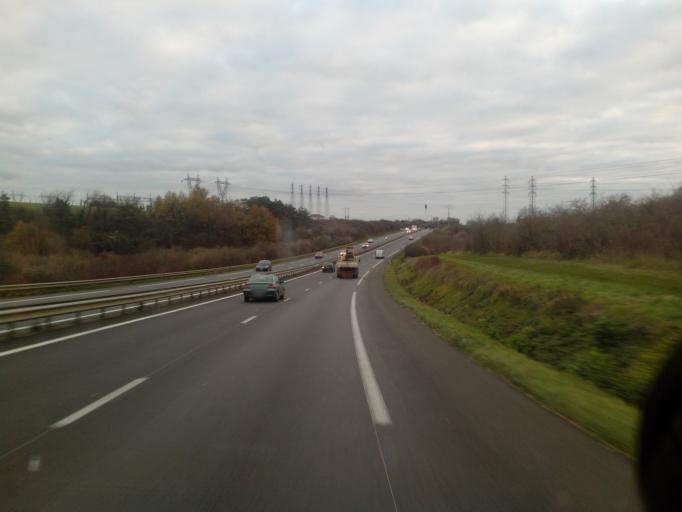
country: FR
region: Poitou-Charentes
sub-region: Departement de la Vienne
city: Montamise
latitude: 46.6036
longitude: 0.3930
